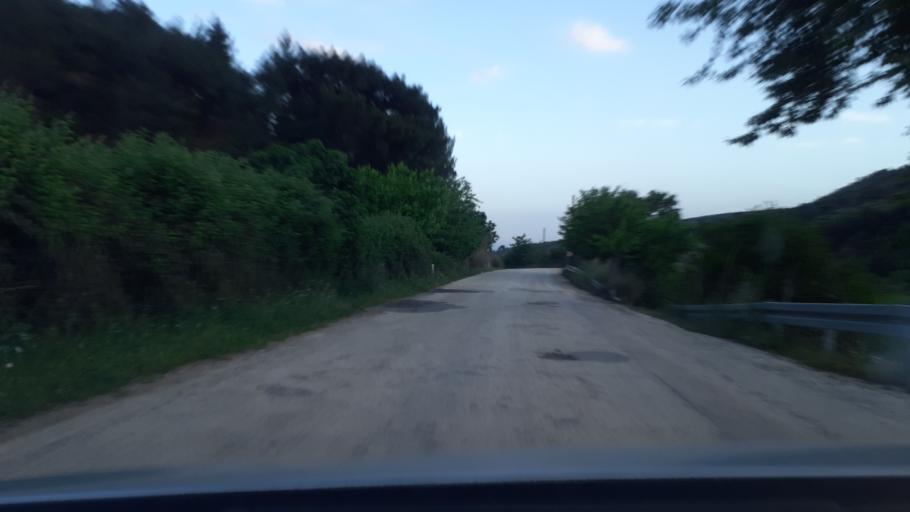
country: TR
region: Hatay
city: Kirikhan
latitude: 36.5200
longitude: 36.3182
